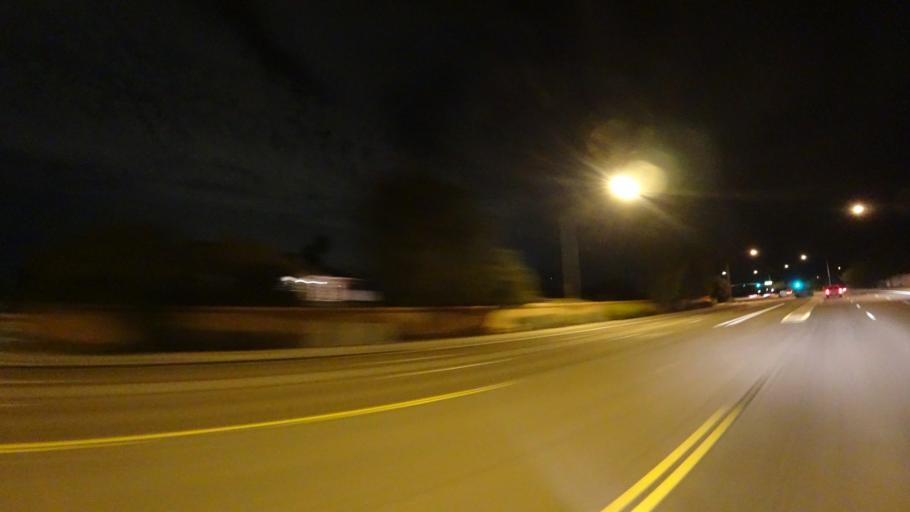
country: US
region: Arizona
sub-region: Maricopa County
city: Mesa
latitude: 33.4560
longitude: -111.7876
